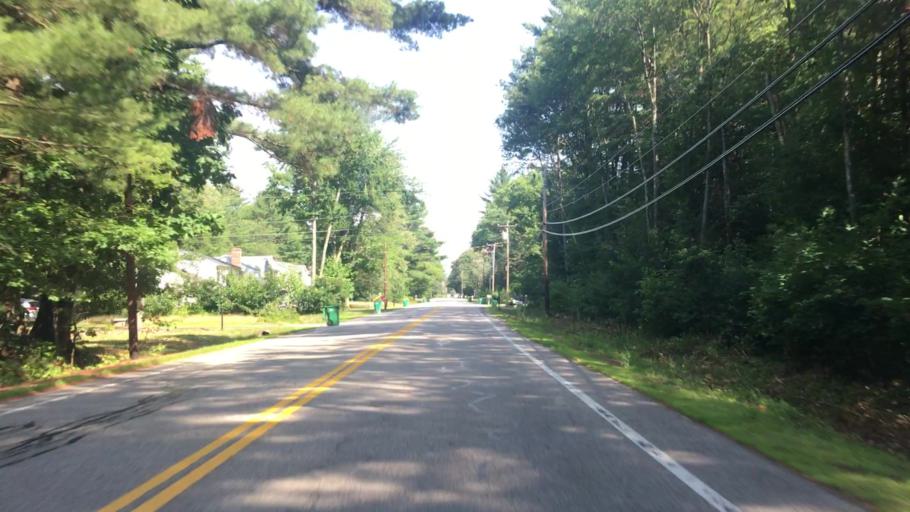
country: US
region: New Hampshire
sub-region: Strafford County
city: Rochester
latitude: 43.2805
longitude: -70.9696
